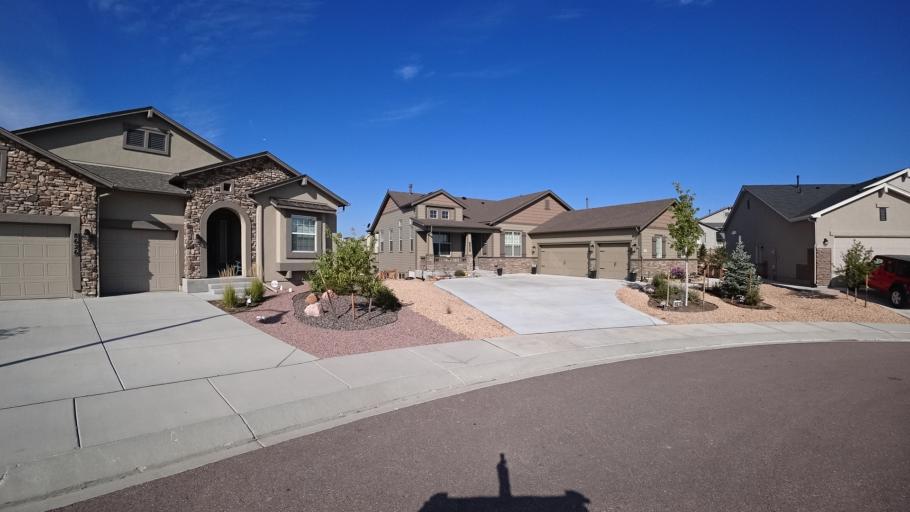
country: US
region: Colorado
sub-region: El Paso County
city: Cimarron Hills
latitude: 38.9295
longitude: -104.6677
